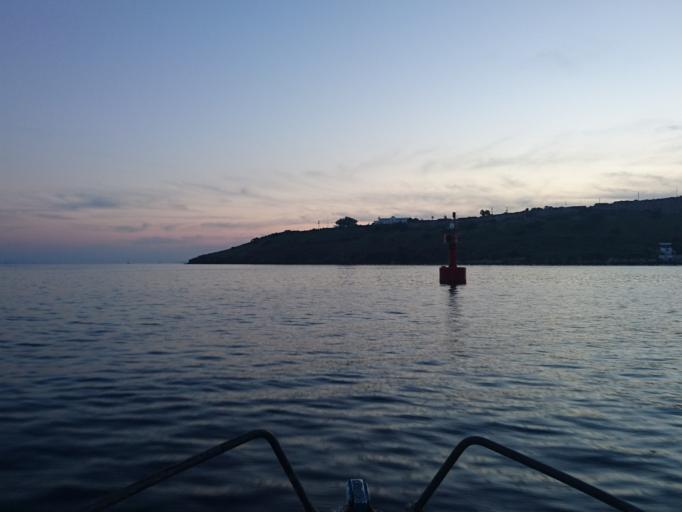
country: TR
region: Mugla
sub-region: Bodrum
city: Bodrum
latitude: 37.0291
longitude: 27.4225
